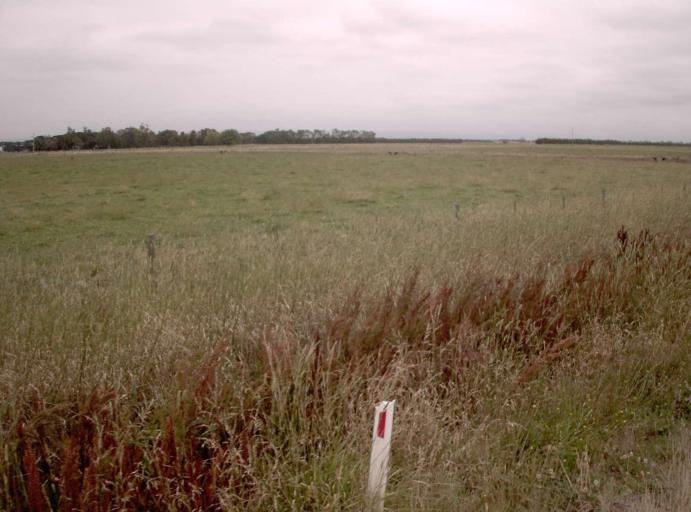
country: AU
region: Victoria
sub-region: Wellington
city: Heyfield
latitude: -38.0961
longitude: 146.7729
